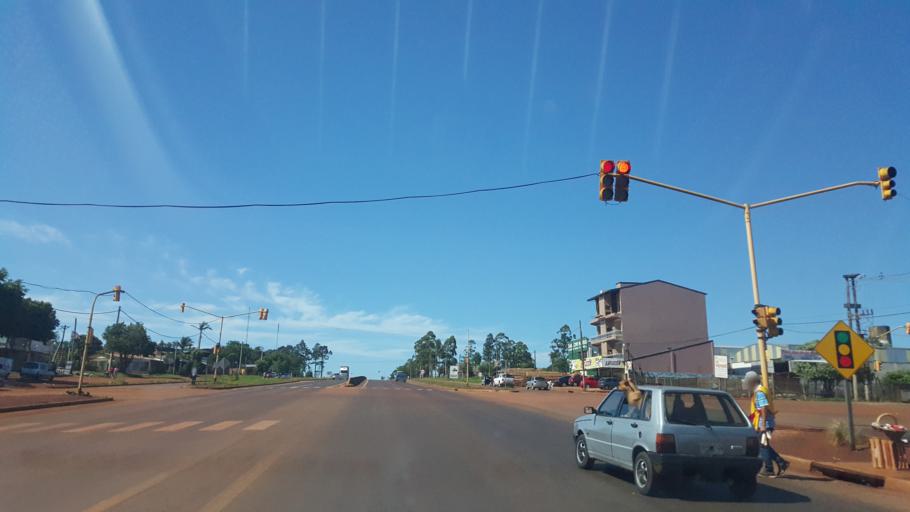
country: AR
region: Misiones
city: Garupa
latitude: -27.4662
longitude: -55.8630
